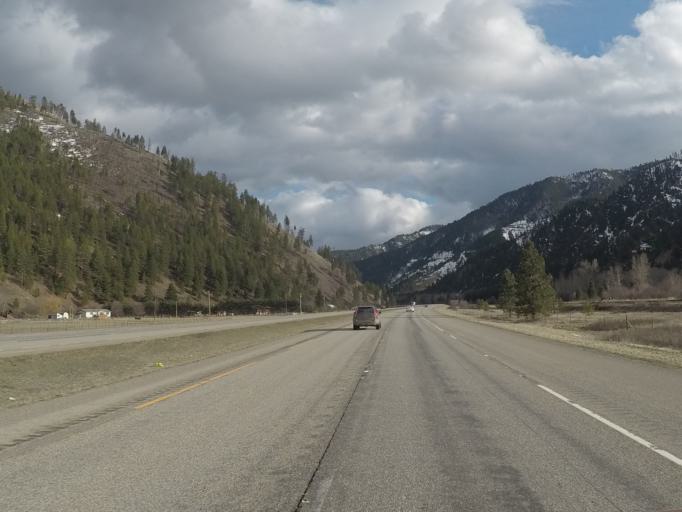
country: US
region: Montana
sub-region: Missoula County
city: Clinton
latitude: 46.7378
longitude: -113.6994
